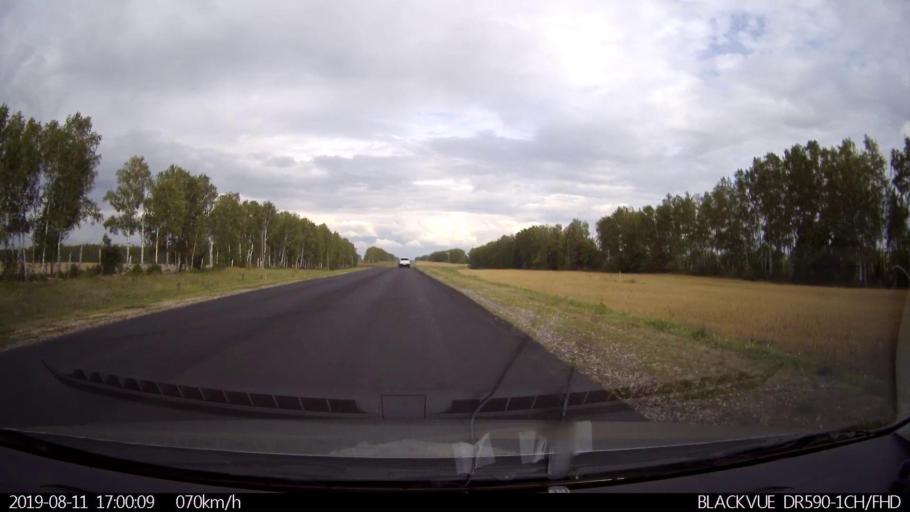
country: RU
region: Ulyanovsk
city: Mayna
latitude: 54.3110
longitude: 47.6744
